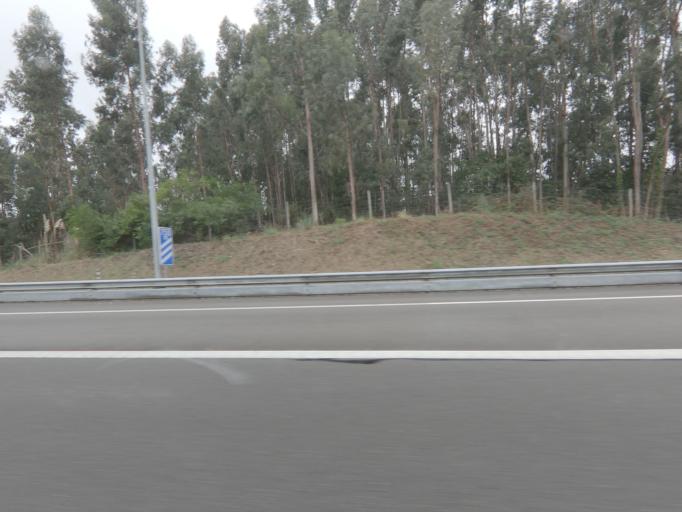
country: PT
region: Porto
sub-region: Maia
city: Leca do Bailio
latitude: 41.2030
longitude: -8.6190
